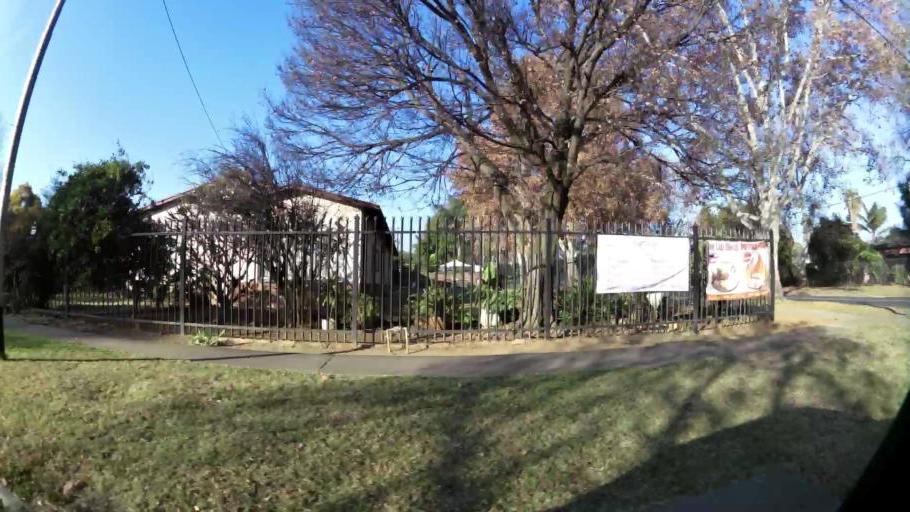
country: ZA
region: Gauteng
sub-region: City of Tshwane Metropolitan Municipality
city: Pretoria
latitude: -25.7094
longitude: 28.1806
